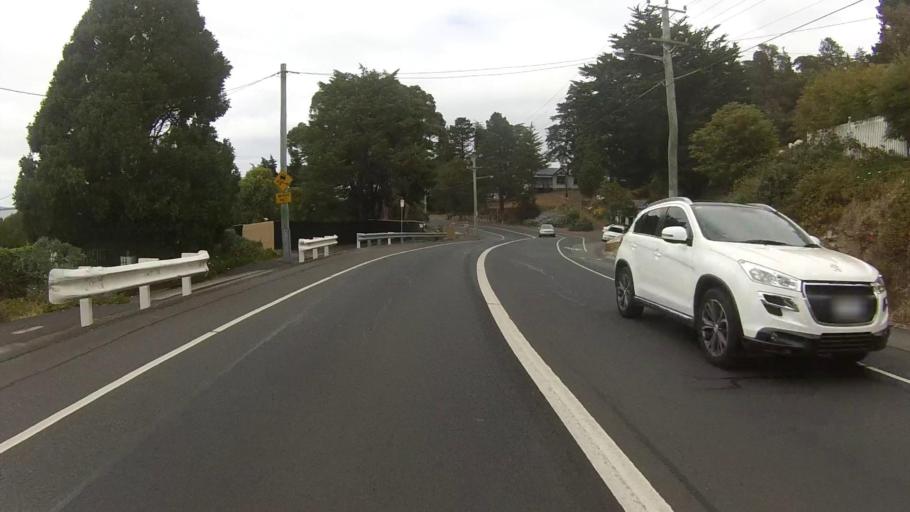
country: AU
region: Tasmania
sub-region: Kingborough
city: Taroona
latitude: -42.9257
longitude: 147.3607
